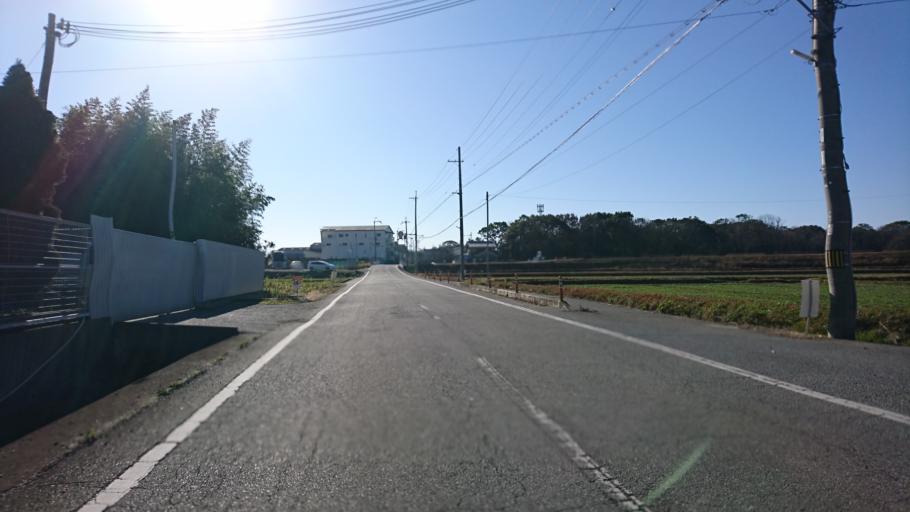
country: JP
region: Hyogo
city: Miki
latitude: 34.7569
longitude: 134.9254
